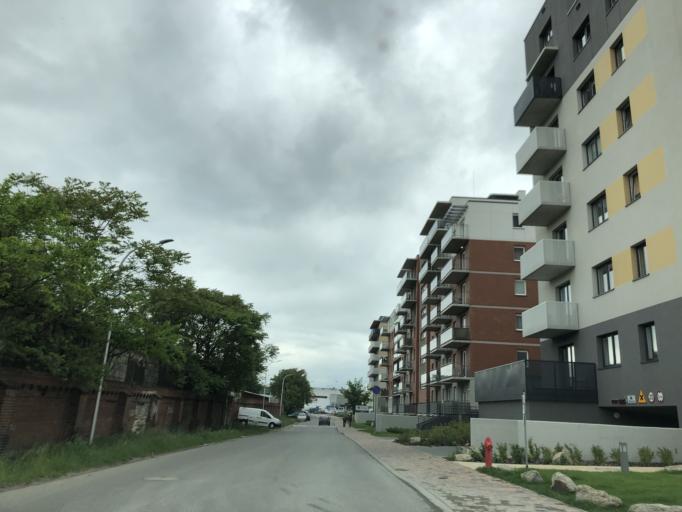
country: PL
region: Lower Silesian Voivodeship
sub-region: Powiat wroclawski
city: Wroclaw
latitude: 51.1281
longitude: 17.0399
